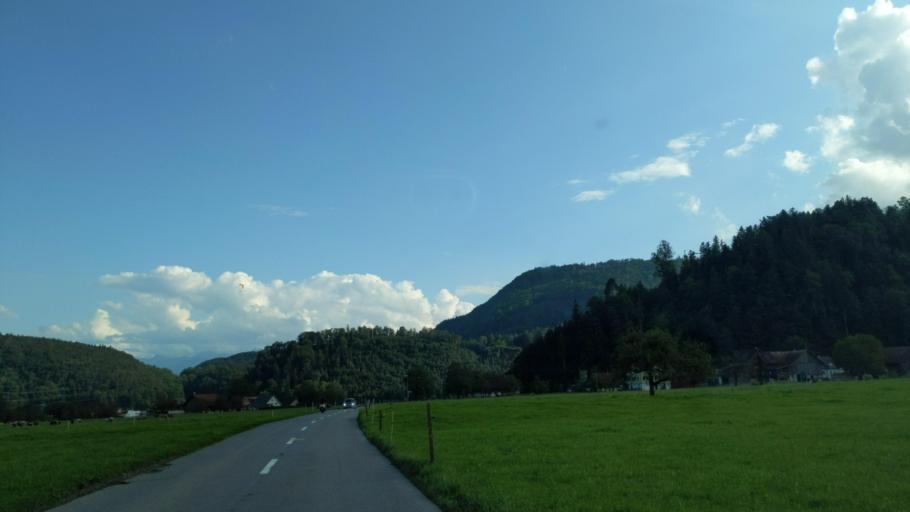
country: CH
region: Saint Gallen
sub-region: Wahlkreis Rheintal
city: Eichberg
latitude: 47.3376
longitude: 9.5330
